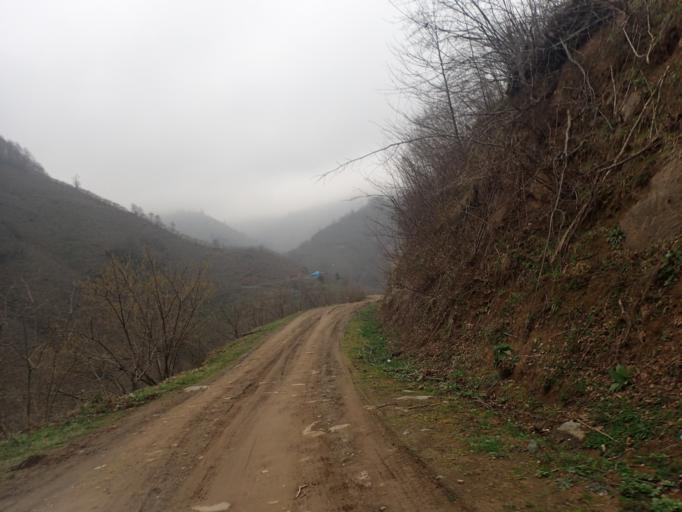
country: TR
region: Ordu
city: Camas
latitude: 40.8984
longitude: 37.5593
